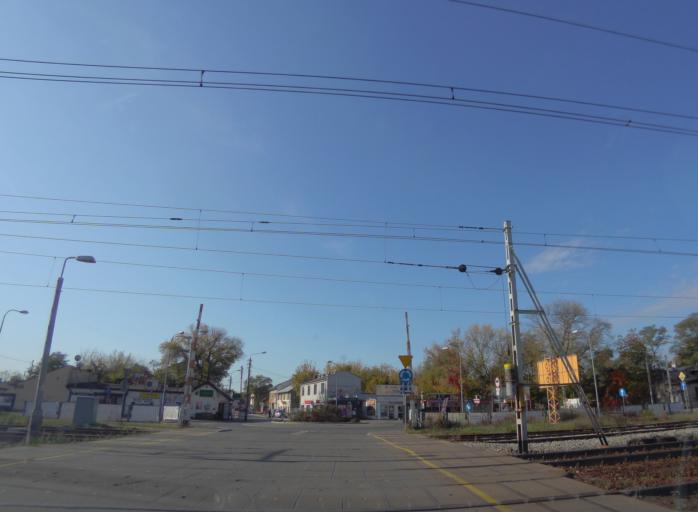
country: PL
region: Masovian Voivodeship
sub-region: Powiat otwocki
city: Jozefow
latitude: 52.1609
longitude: 21.2122
